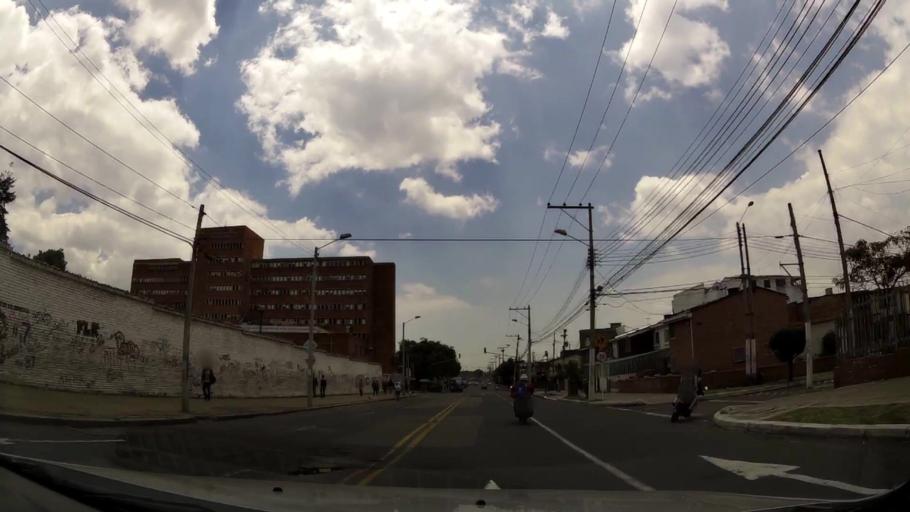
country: CO
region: Bogota D.C.
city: Bogota
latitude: 4.5768
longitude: -74.0902
